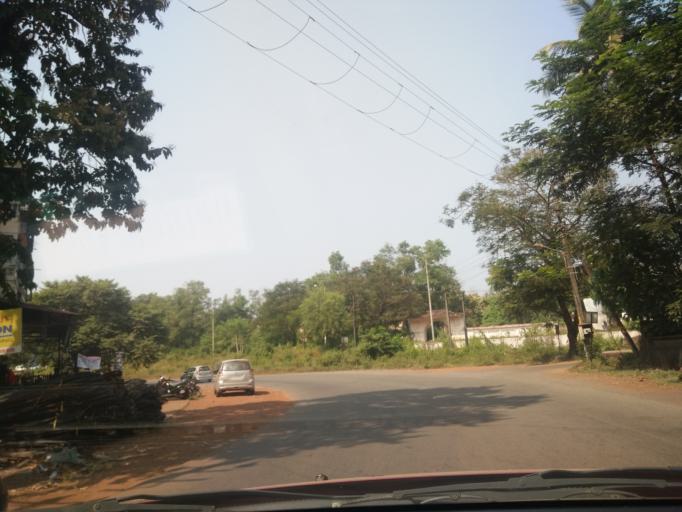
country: IN
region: Goa
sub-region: North Goa
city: Sanquelim
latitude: 15.5582
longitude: 74.0200
